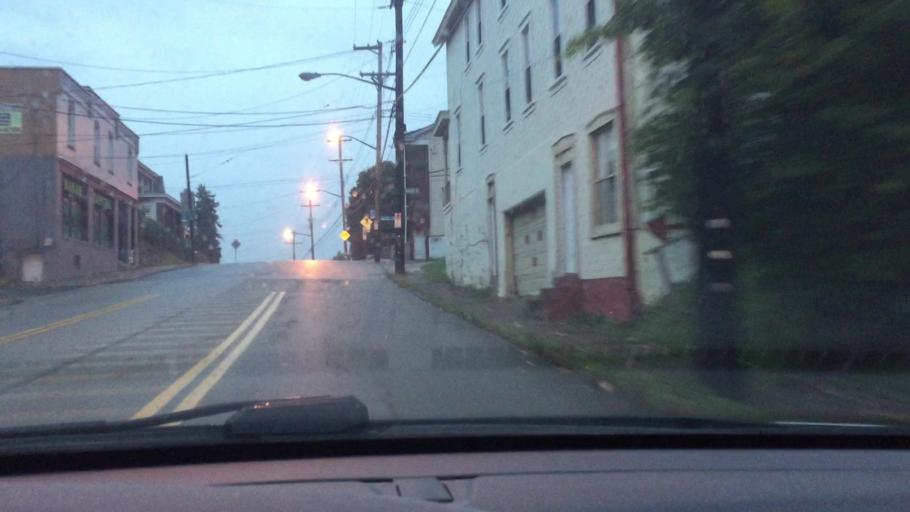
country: US
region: Pennsylvania
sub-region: Allegheny County
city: Crafton
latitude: 40.4418
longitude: -80.0455
